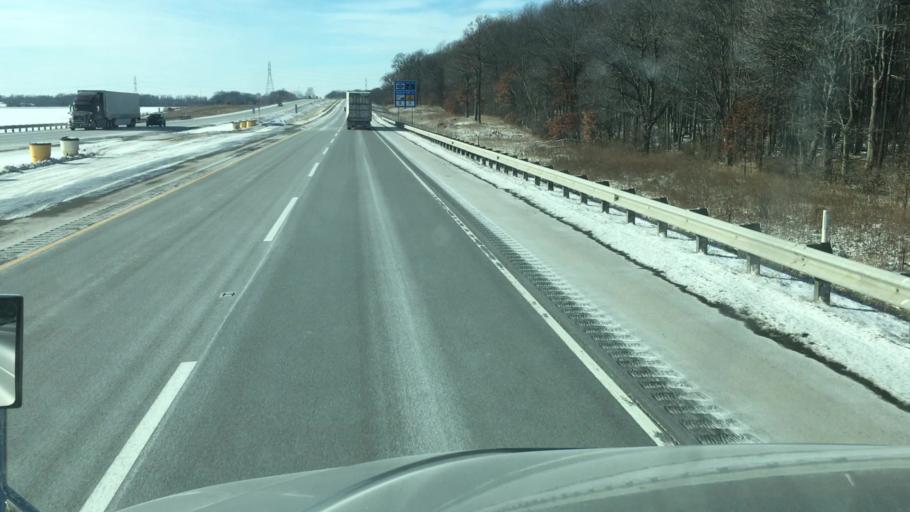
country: US
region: Indiana
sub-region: Saint Joseph County
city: Granger
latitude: 41.7339
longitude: -86.1193
